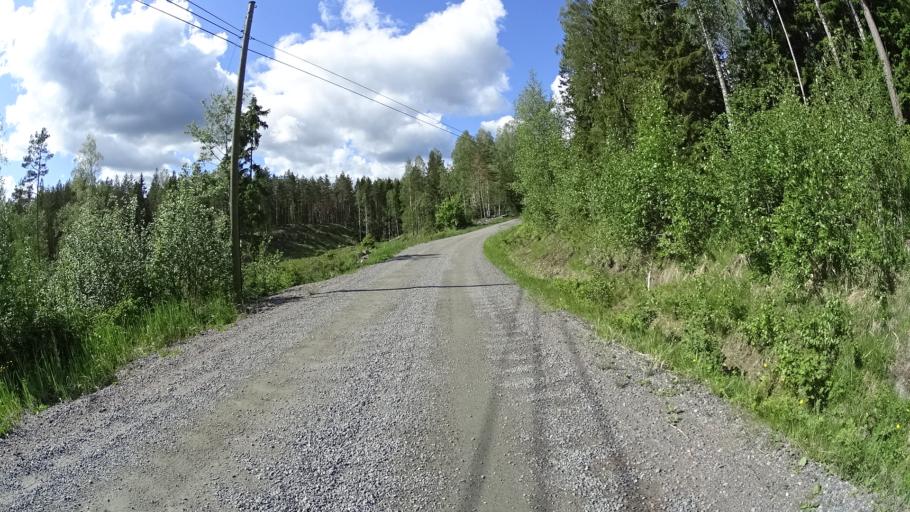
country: FI
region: Uusimaa
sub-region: Raaseporin
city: Pohja
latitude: 60.1741
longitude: 23.5857
